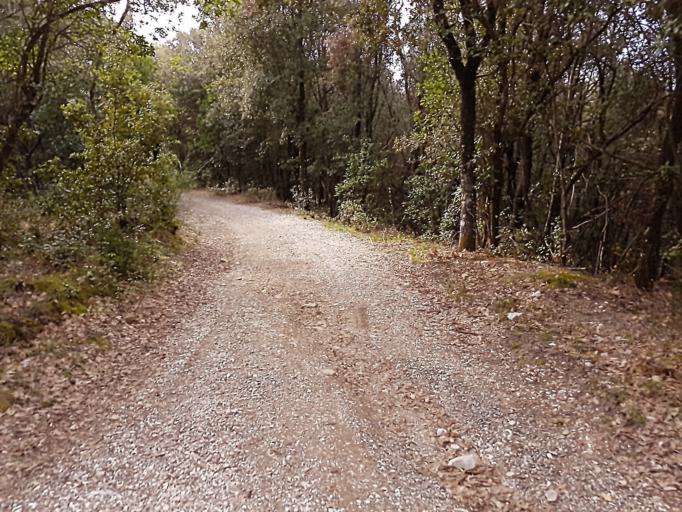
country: IT
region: Umbria
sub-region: Provincia di Perugia
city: Corciano
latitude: 43.1326
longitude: 12.3024
